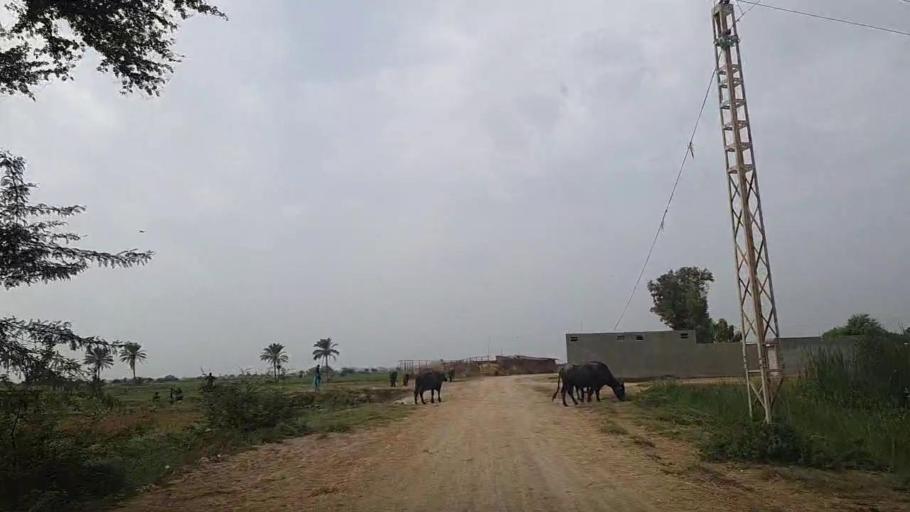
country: PK
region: Sindh
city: Mirpur Batoro
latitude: 24.6076
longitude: 68.1004
